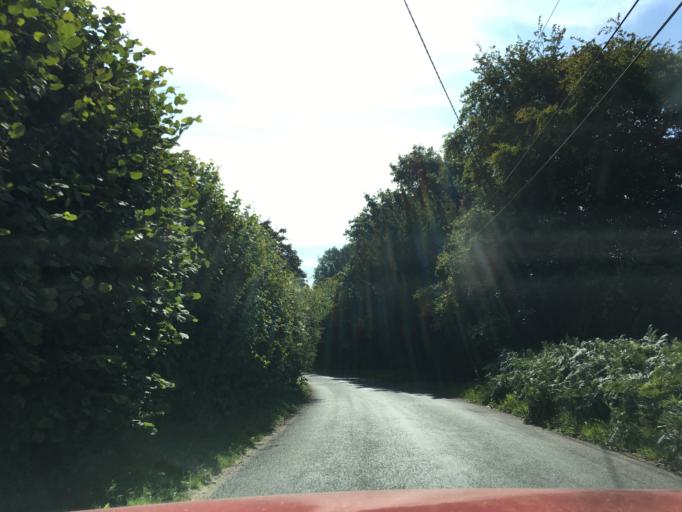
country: GB
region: England
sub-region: West Berkshire
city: Kintbury
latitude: 51.3685
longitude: -1.4299
